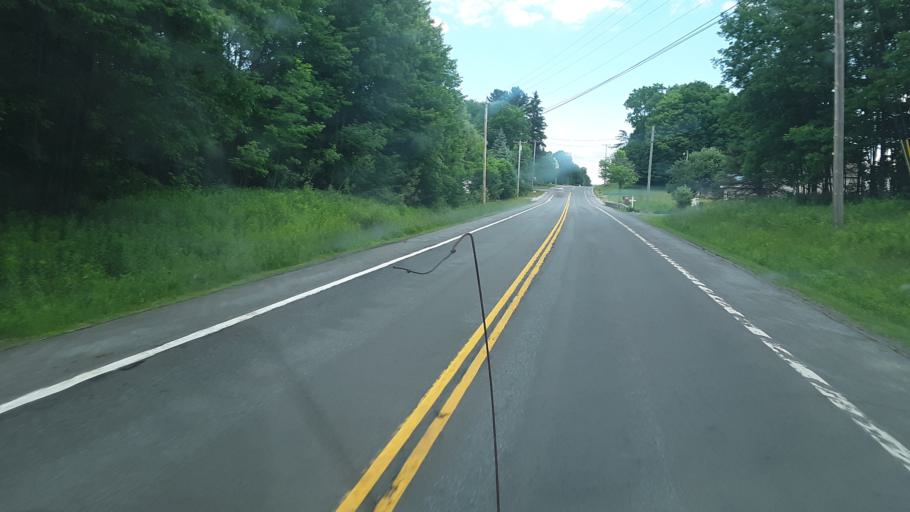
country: US
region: New York
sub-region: Oneida County
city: Rome
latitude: 43.3474
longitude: -75.4761
